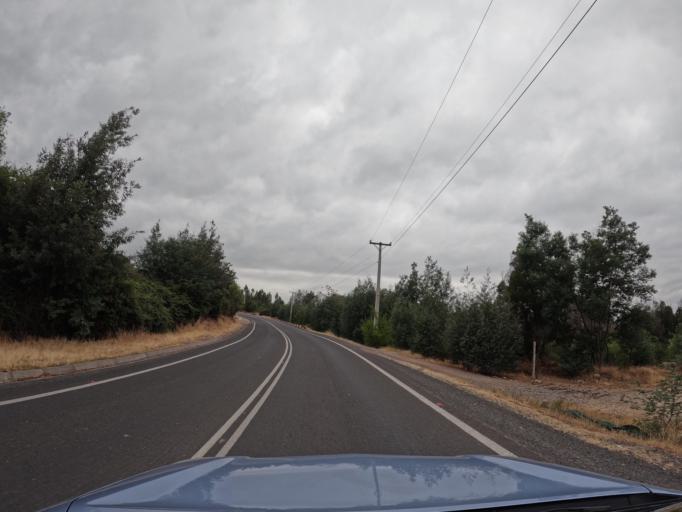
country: CL
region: O'Higgins
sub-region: Provincia de Colchagua
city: Chimbarongo
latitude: -34.7299
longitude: -71.0960
